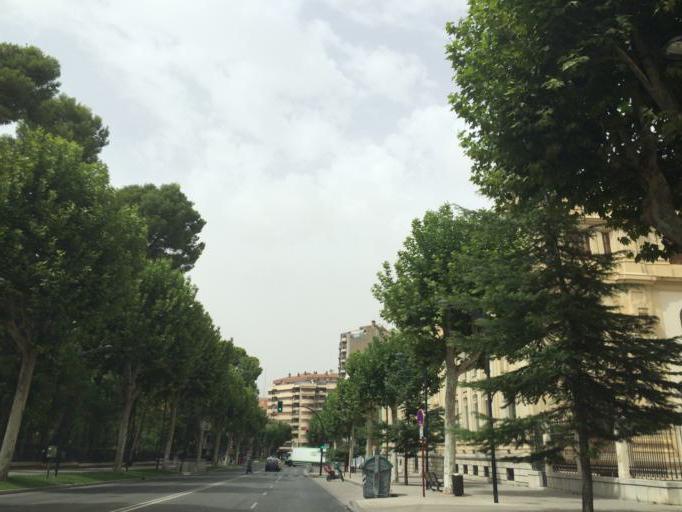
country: ES
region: Castille-La Mancha
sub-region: Provincia de Albacete
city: Albacete
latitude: 38.9886
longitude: -1.8554
